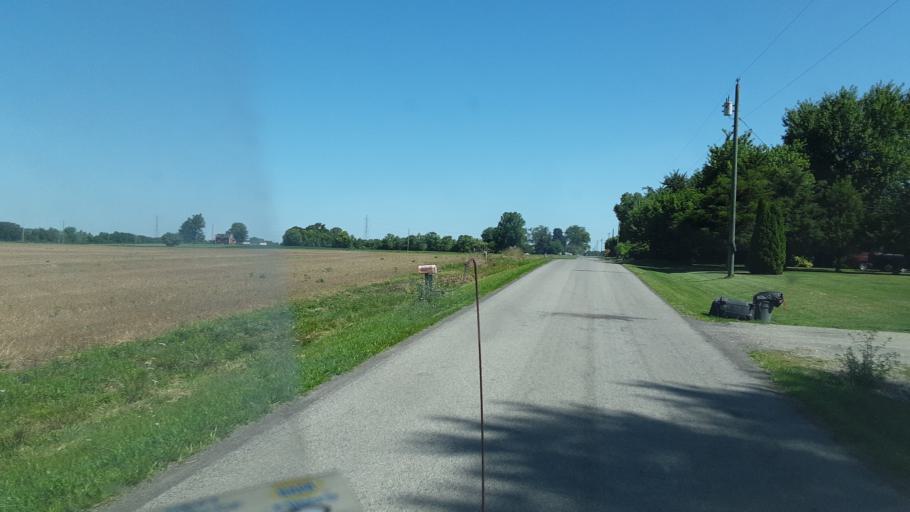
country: US
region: Ohio
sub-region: Union County
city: Richwood
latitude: 40.3459
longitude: -83.3342
